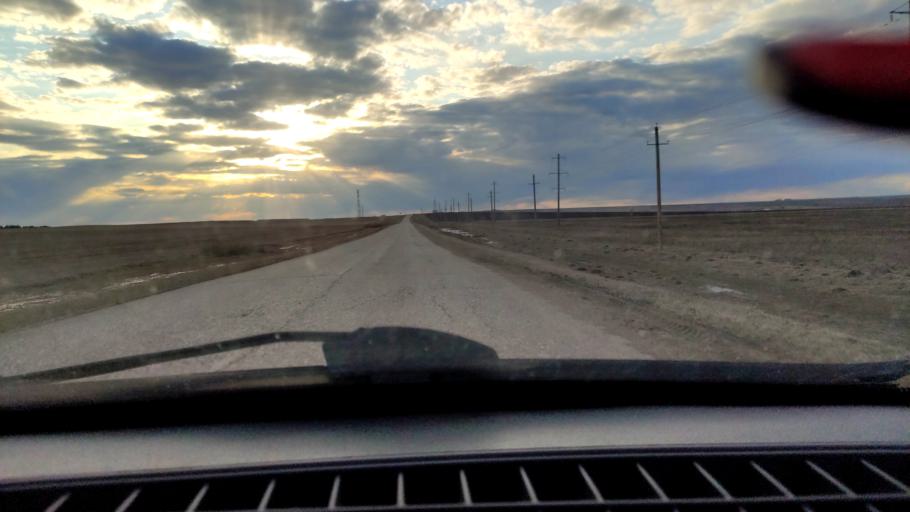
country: RU
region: Bashkortostan
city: Tolbazy
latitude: 54.0096
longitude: 55.7475
